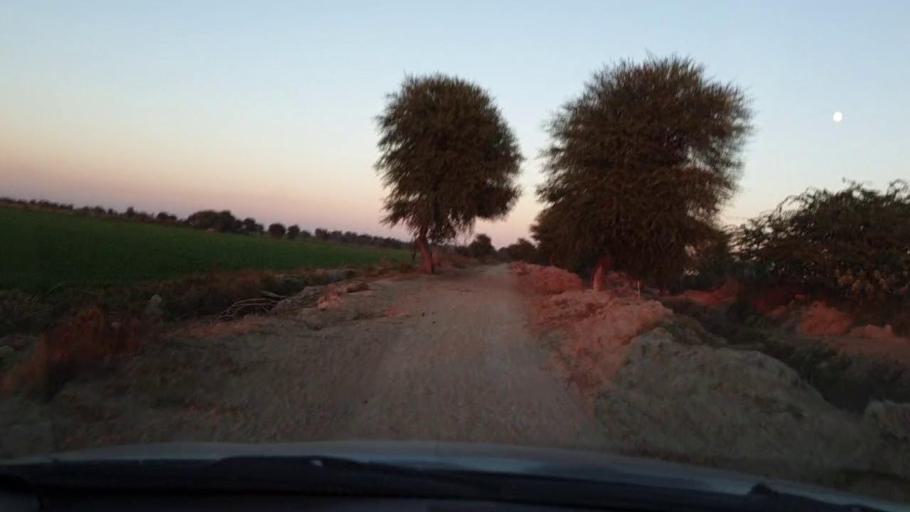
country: PK
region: Sindh
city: Jhol
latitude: 25.9127
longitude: 68.8859
